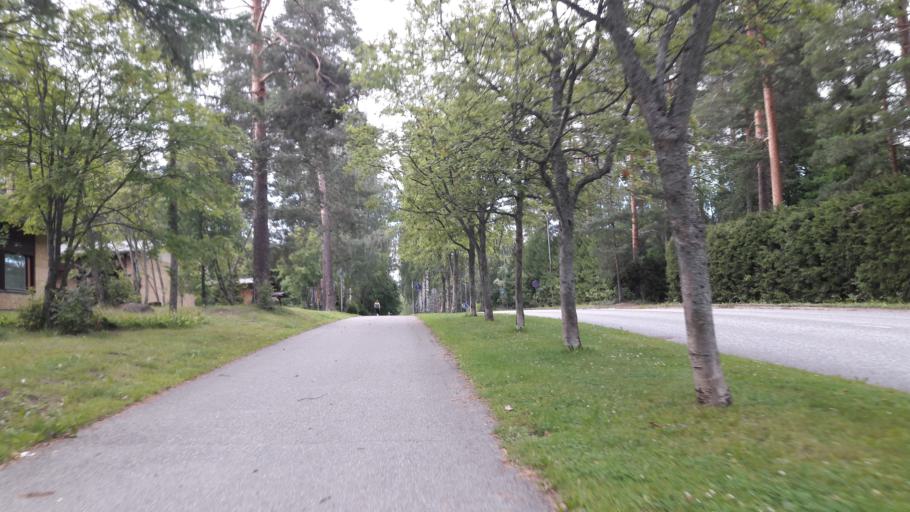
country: FI
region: North Karelia
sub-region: Joensuu
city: Joensuu
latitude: 62.5824
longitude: 29.8043
